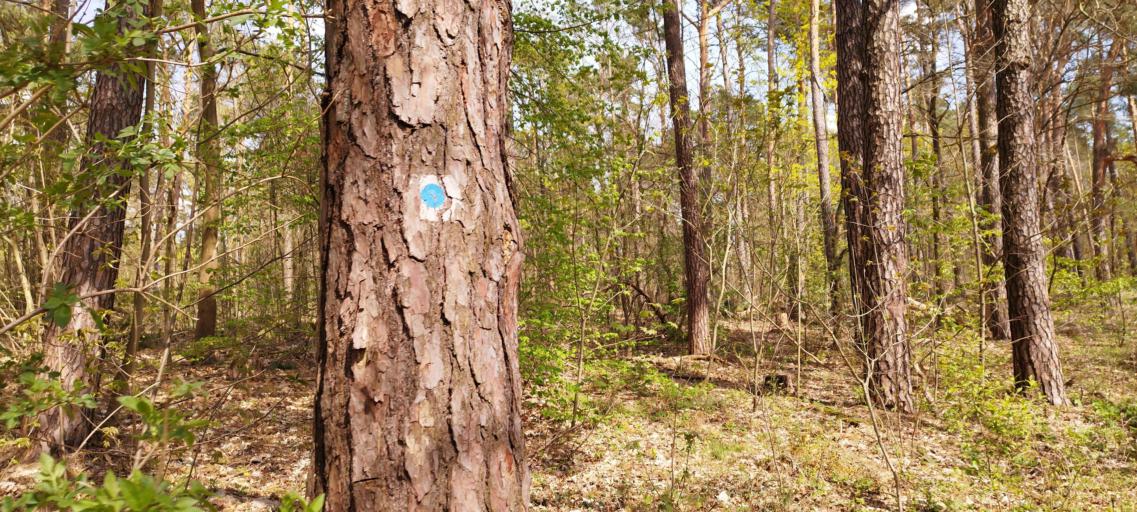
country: DE
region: Brandenburg
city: Erkner
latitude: 52.4202
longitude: 13.7653
